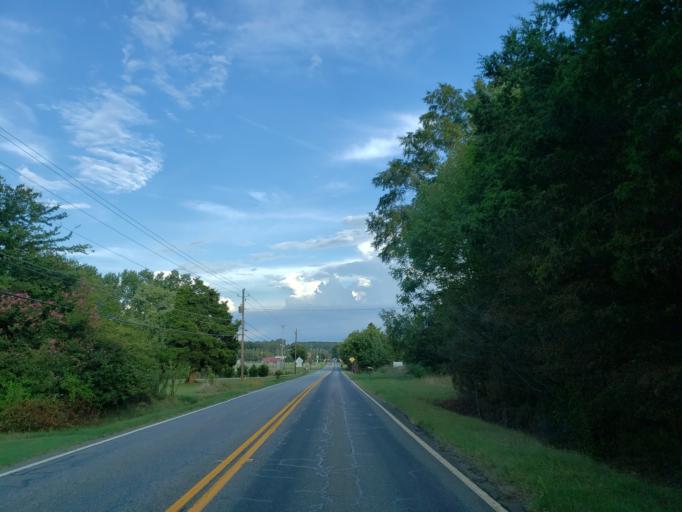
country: US
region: Georgia
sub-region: Bartow County
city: Cartersville
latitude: 34.2354
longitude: -84.8695
